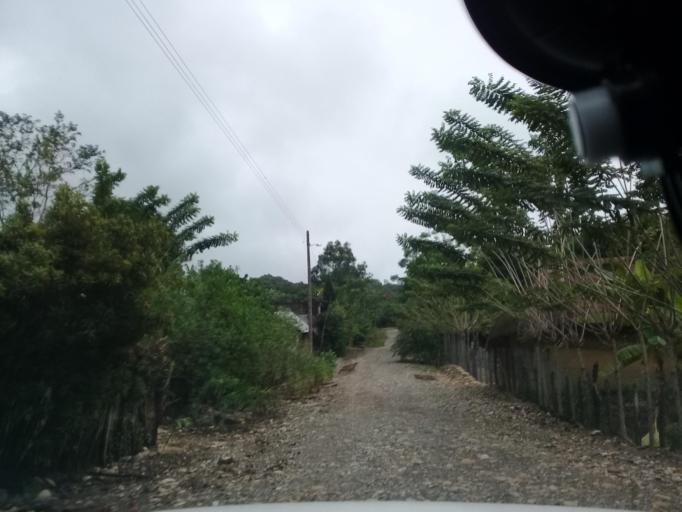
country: MX
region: Veracruz
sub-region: Chalma
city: San Pedro Coyutla
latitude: 21.2230
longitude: -98.4272
